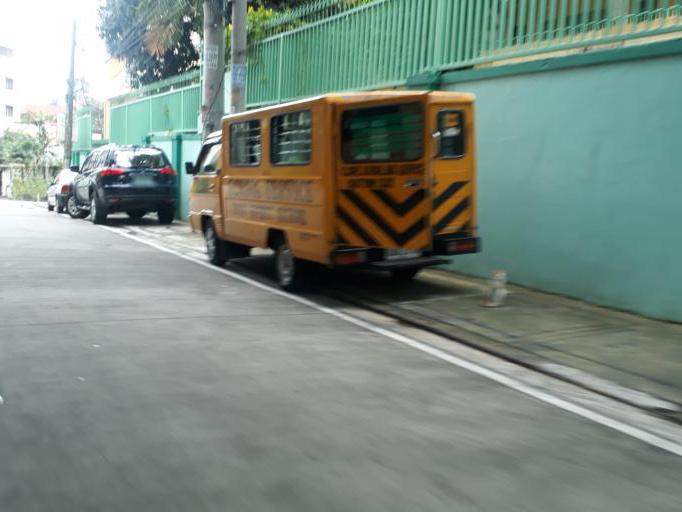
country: PH
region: Metro Manila
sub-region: San Juan
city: San Juan
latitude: 14.6226
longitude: 121.0403
